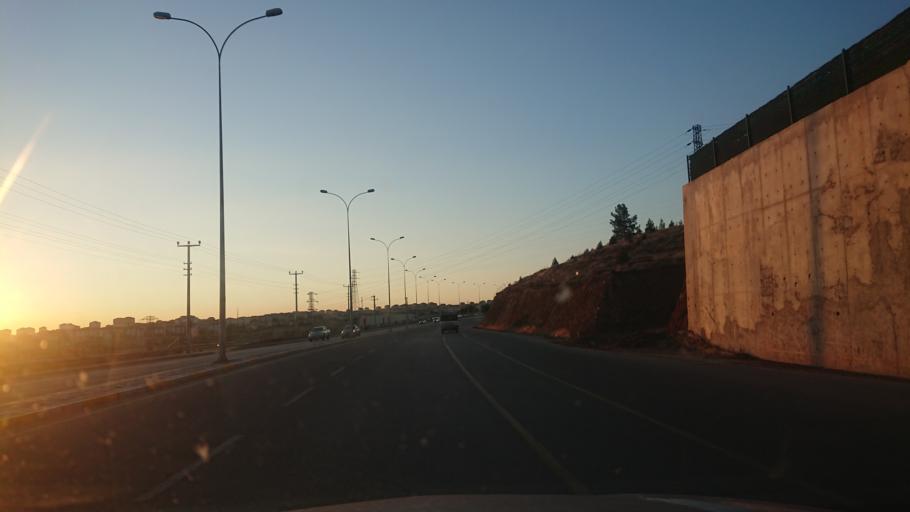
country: TR
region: Aksaray
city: Aksaray
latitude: 38.4049
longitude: 34.0134
